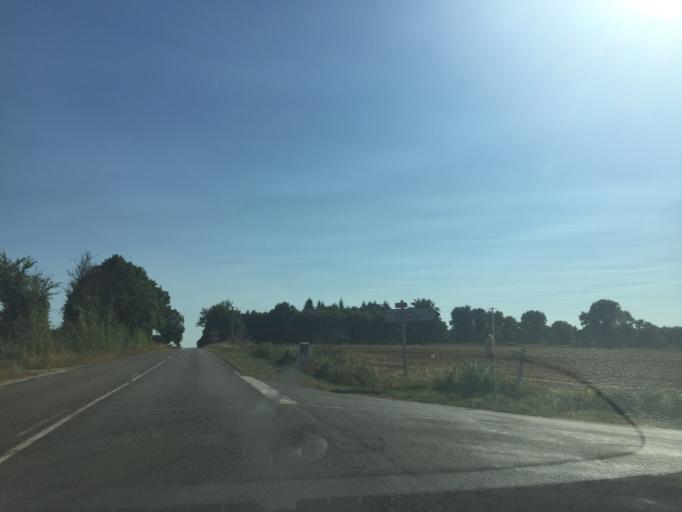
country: FR
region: Poitou-Charentes
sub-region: Departement des Deux-Sevres
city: Melle
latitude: 46.2473
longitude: -0.1011
